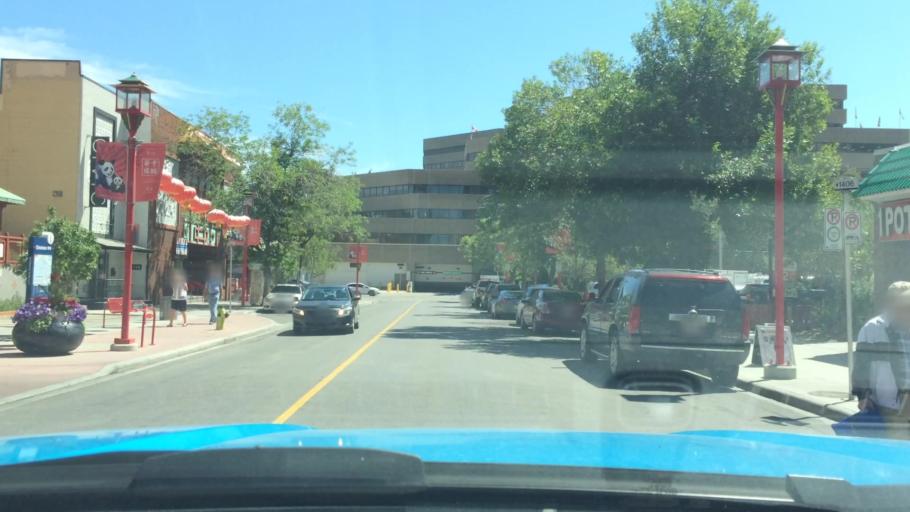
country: CA
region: Alberta
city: Calgary
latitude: 51.0503
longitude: -114.0617
